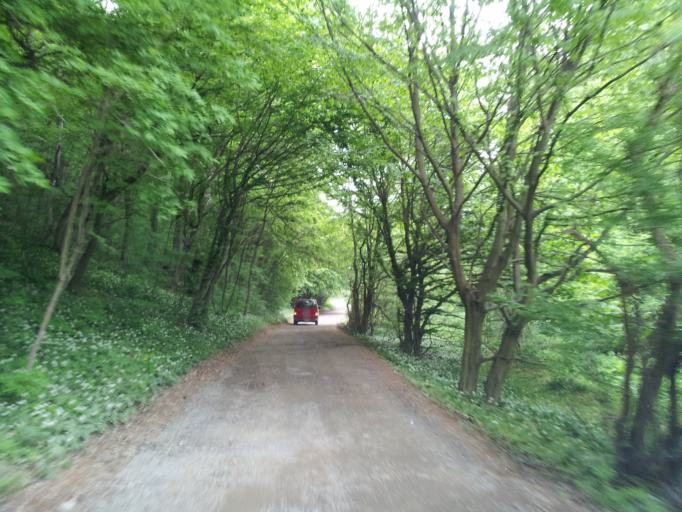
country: HU
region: Baranya
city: Hosszuheteny
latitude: 46.1832
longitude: 18.3529
